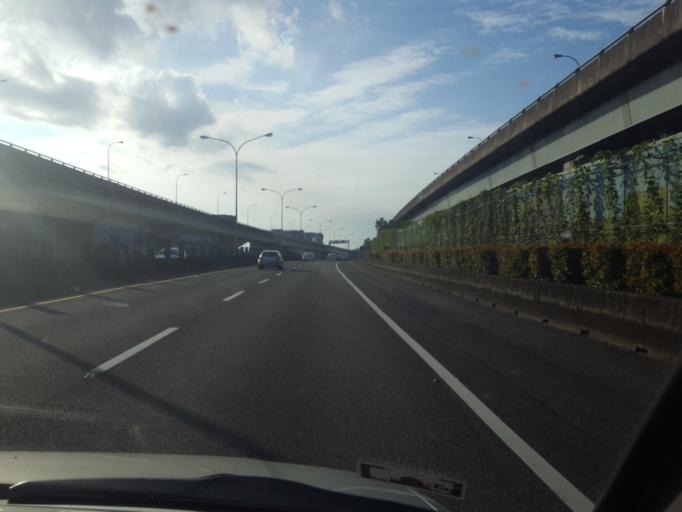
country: TW
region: Taipei
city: Taipei
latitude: 25.0643
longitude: 121.5931
